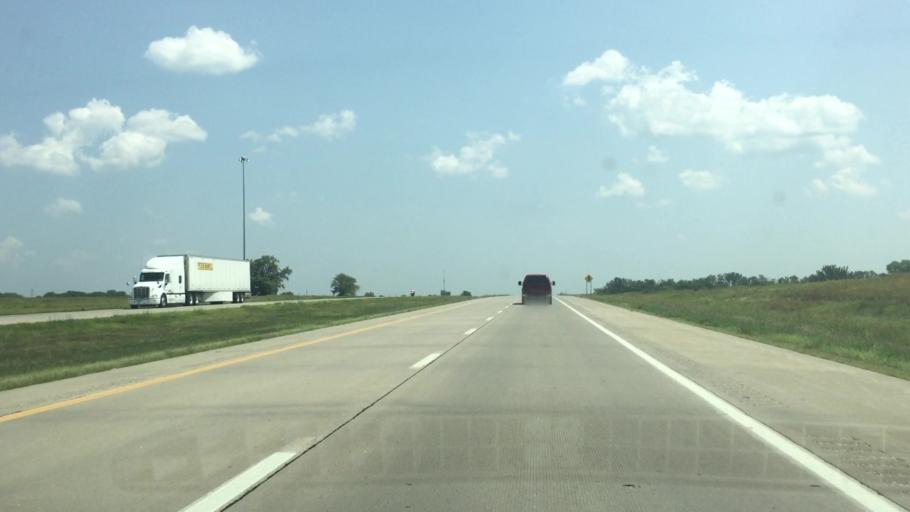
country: US
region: Kansas
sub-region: Franklin County
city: Wellsville
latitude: 38.7047
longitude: -95.0733
